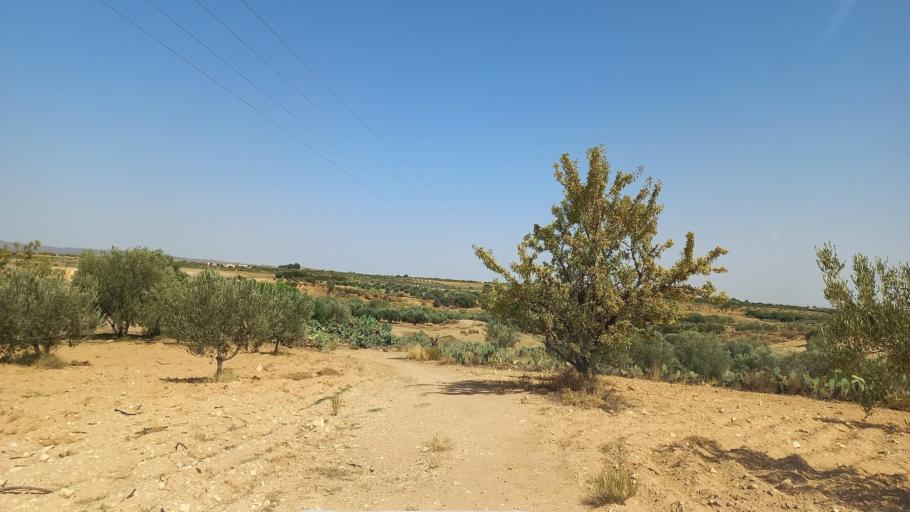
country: TN
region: Al Qasrayn
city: Kasserine
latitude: 35.2253
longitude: 9.0451
